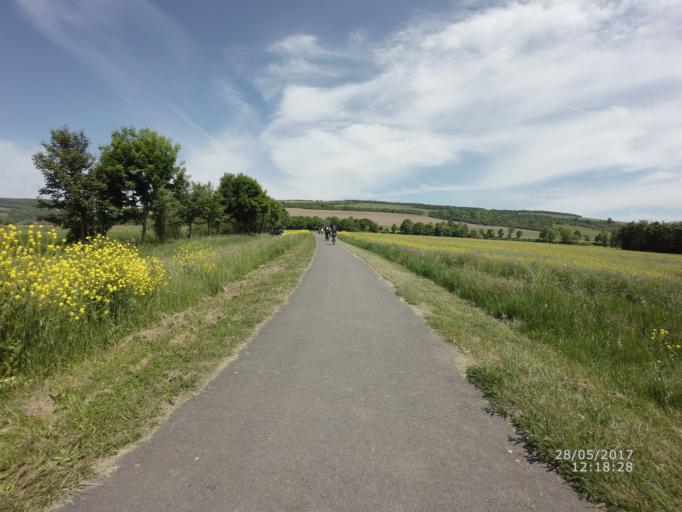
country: DE
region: Thuringia
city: Etzleben
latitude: 51.2805
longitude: 11.1749
